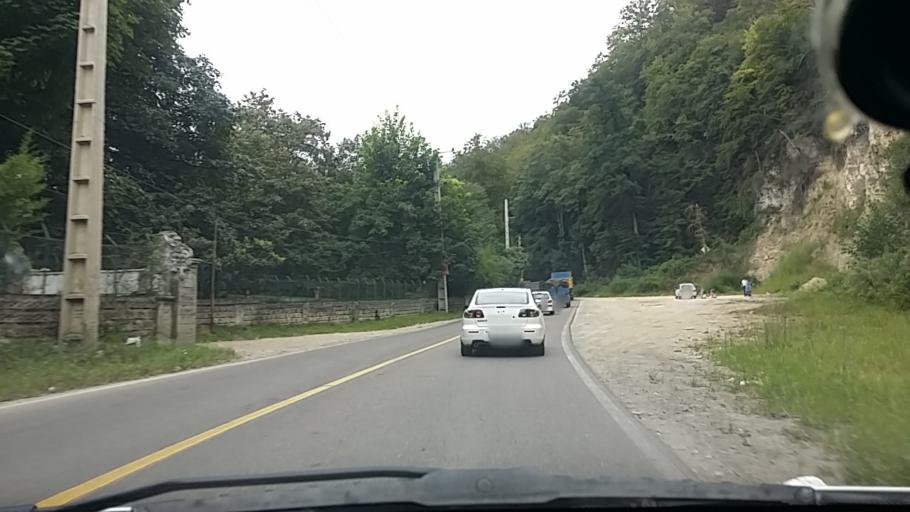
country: IR
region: Mazandaran
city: Chalus
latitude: 36.6085
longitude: 51.3867
